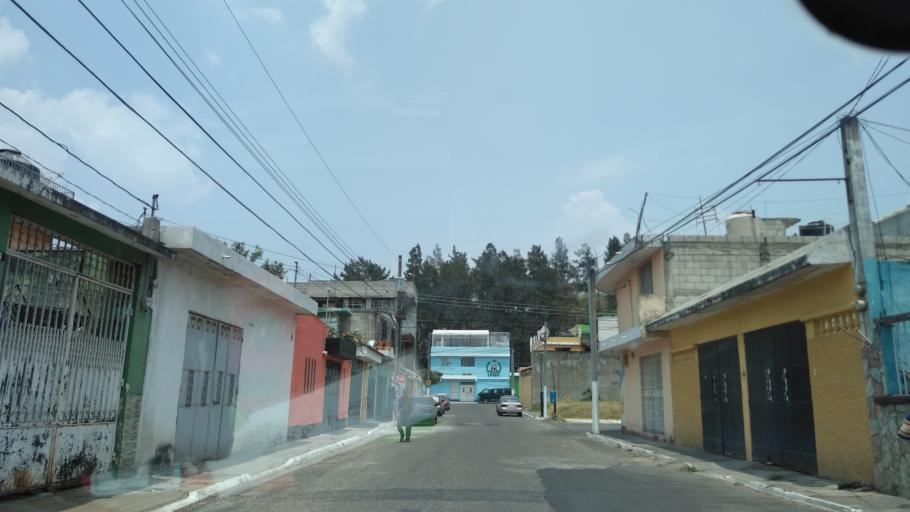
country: GT
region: Guatemala
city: Petapa
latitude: 14.5225
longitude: -90.5420
